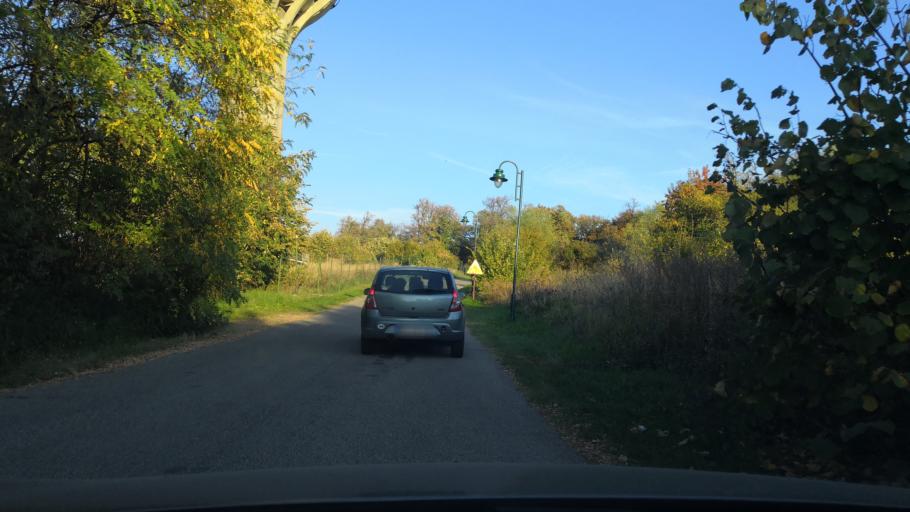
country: RS
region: Autonomna Pokrajina Vojvodina
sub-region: Sremski Okrug
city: Irig
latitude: 45.1581
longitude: 19.8609
